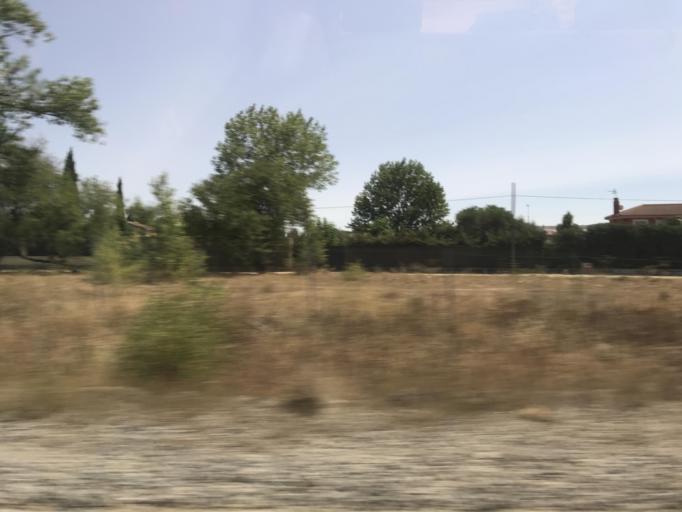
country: ES
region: Castille and Leon
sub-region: Provincia de Valladolid
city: Cubillas de Santa Marta
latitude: 41.8114
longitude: -4.5776
